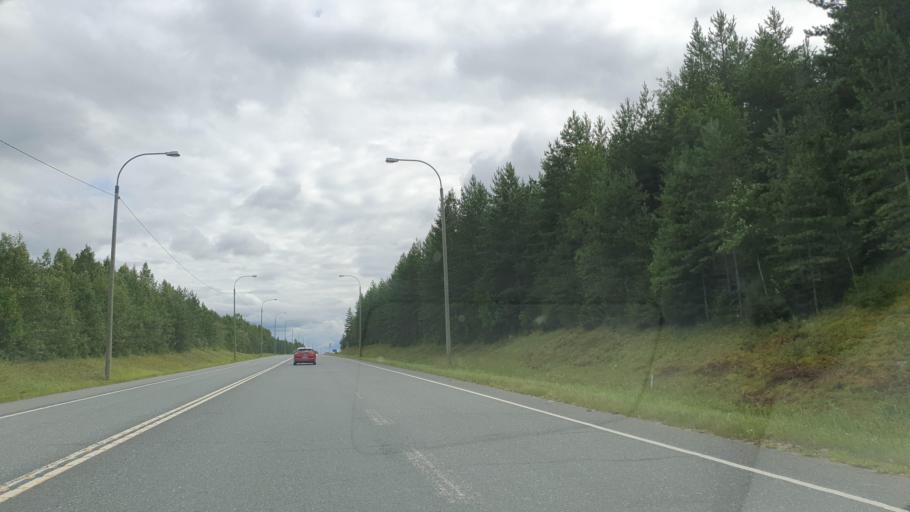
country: FI
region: Northern Savo
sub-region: Ylae-Savo
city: Iisalmi
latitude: 63.5866
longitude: 27.2286
